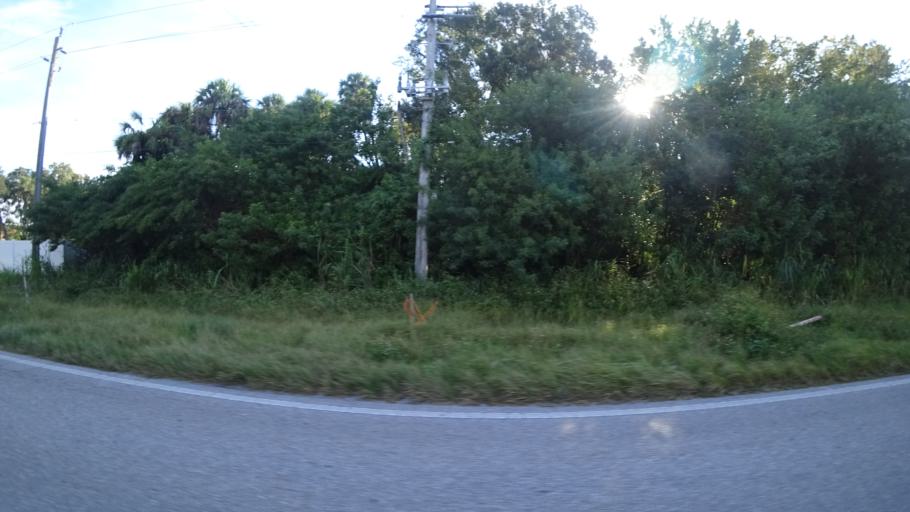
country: US
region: Florida
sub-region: Manatee County
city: Samoset
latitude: 27.4715
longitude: -82.5302
